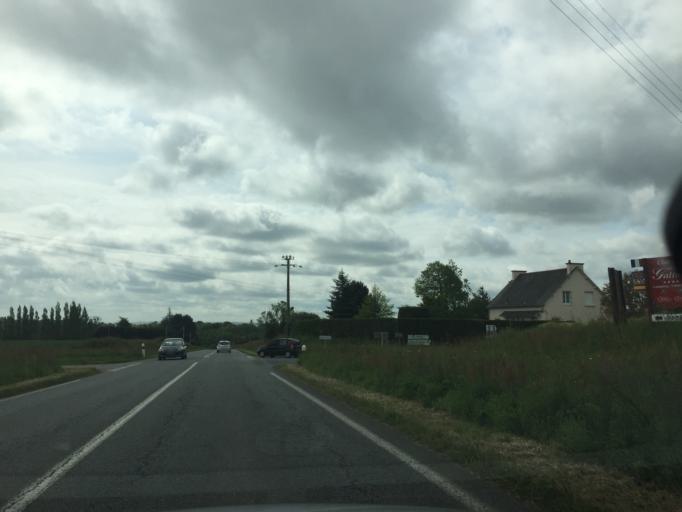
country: FR
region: Brittany
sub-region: Departement des Cotes-d'Armor
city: Saint-Cast-le-Guildo
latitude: 48.5916
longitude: -2.2471
